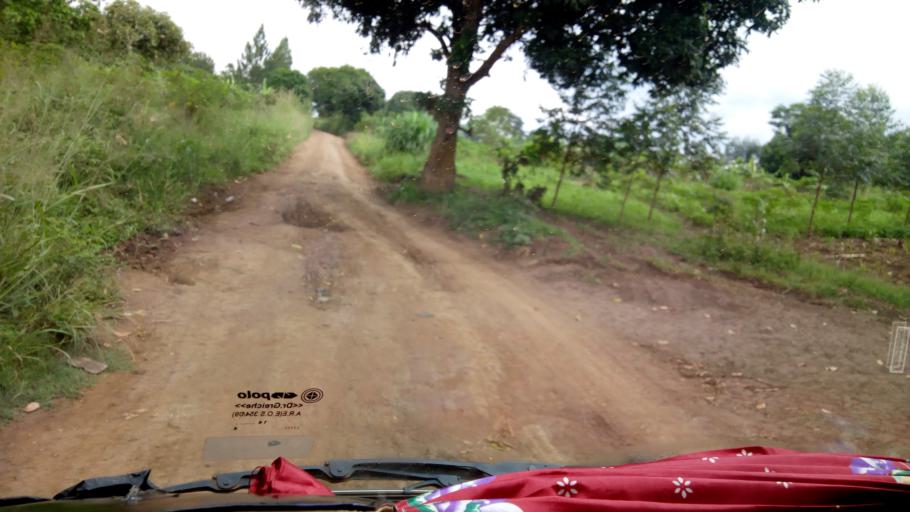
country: UG
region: Central Region
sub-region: Kiboga District
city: Kiboga
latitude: 0.7356
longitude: 31.7385
